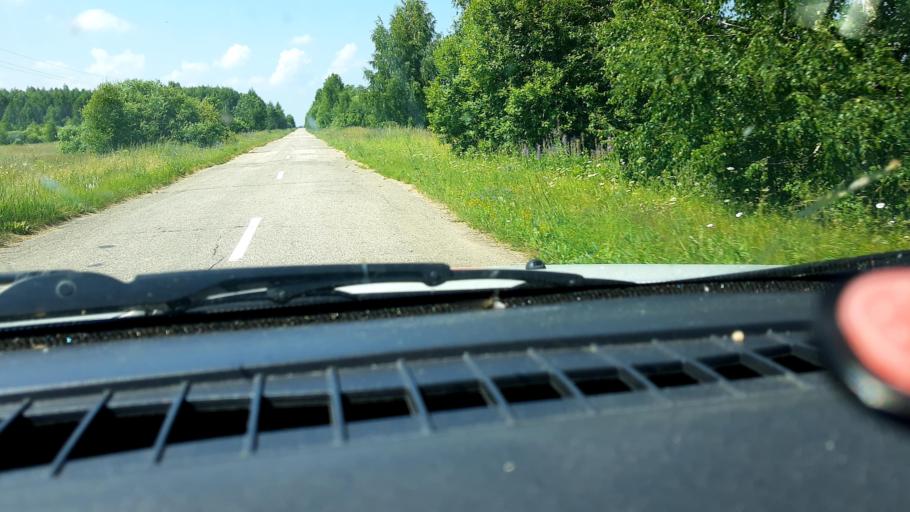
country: RU
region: Nizjnij Novgorod
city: Sharanga
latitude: 57.0640
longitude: 46.6500
